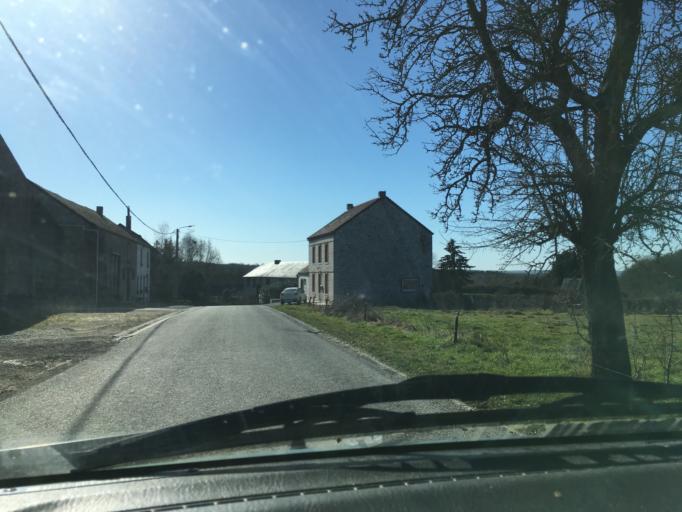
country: BE
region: Wallonia
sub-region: Province de Namur
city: Doische
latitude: 50.1671
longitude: 4.7340
